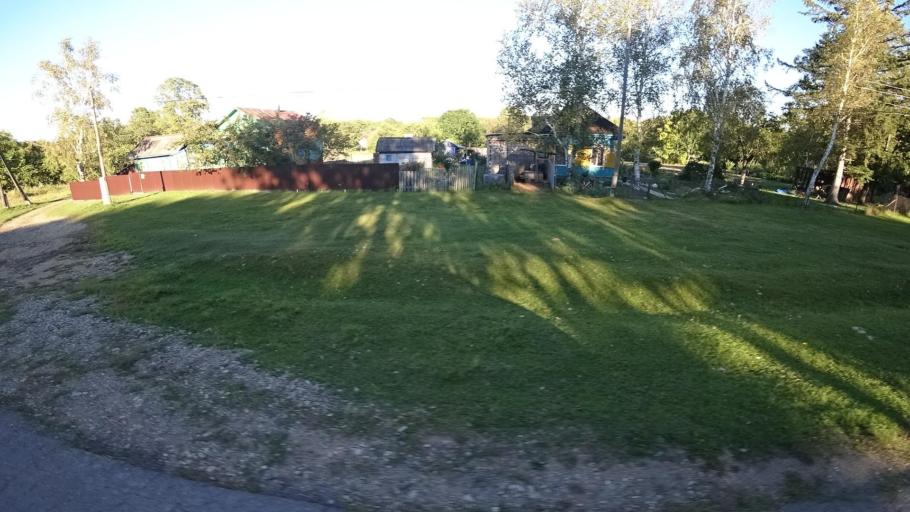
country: RU
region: Primorskiy
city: Kirovskiy
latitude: 44.8287
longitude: 133.5751
